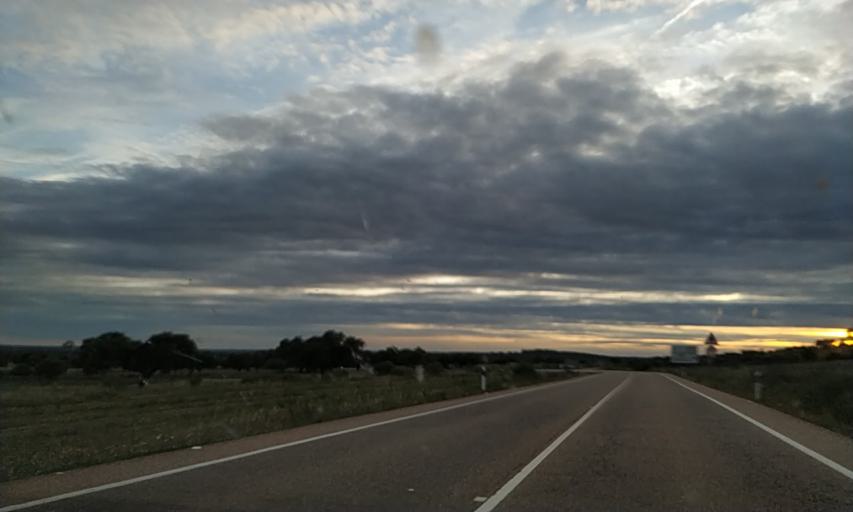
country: ES
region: Extremadura
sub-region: Provincia de Badajoz
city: La Roca de la Sierra
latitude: 39.1087
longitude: -6.7051
